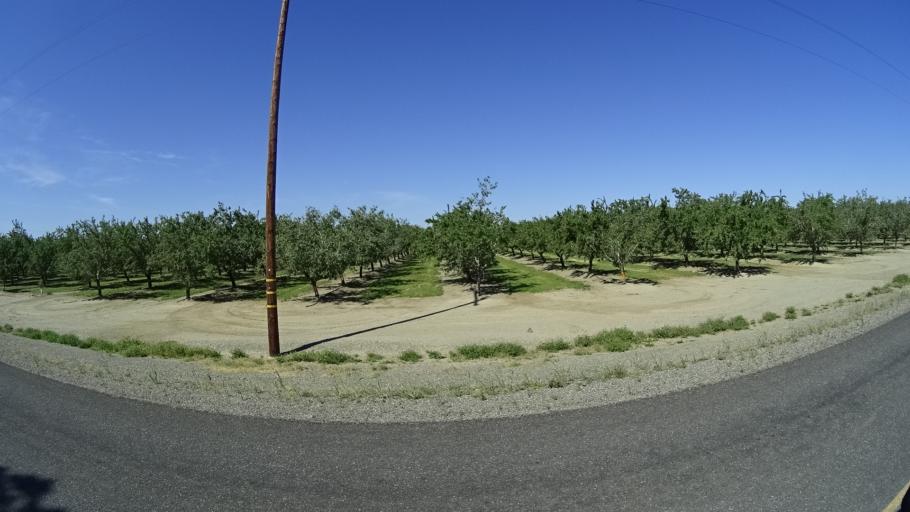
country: US
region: California
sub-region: Glenn County
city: Hamilton City
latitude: 39.6904
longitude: -122.1032
